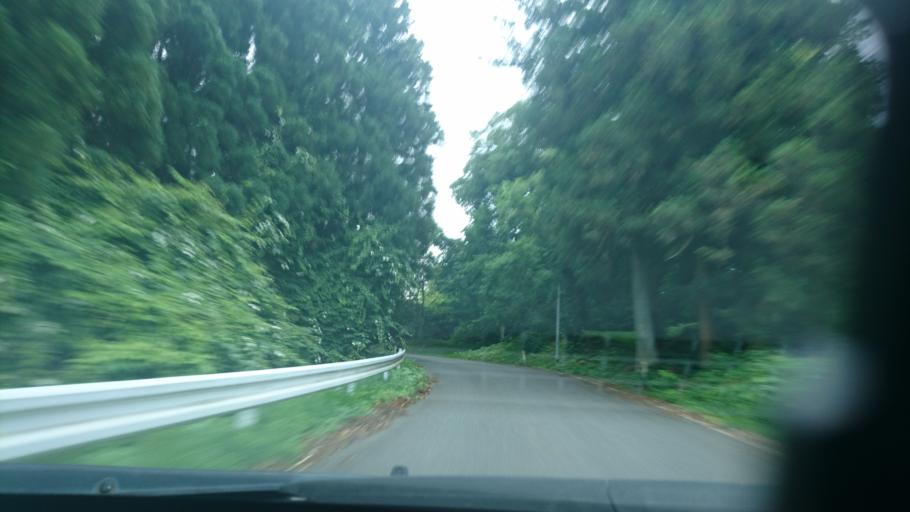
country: JP
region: Iwate
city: Ichinoseki
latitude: 38.8947
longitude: 141.3076
